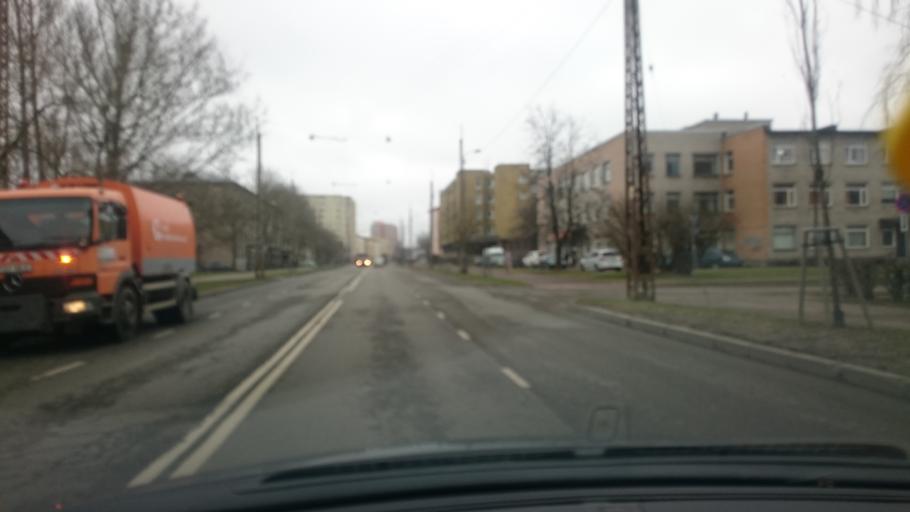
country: EE
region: Harju
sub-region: Tallinna linn
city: Tallinn
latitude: 59.4509
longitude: 24.6955
